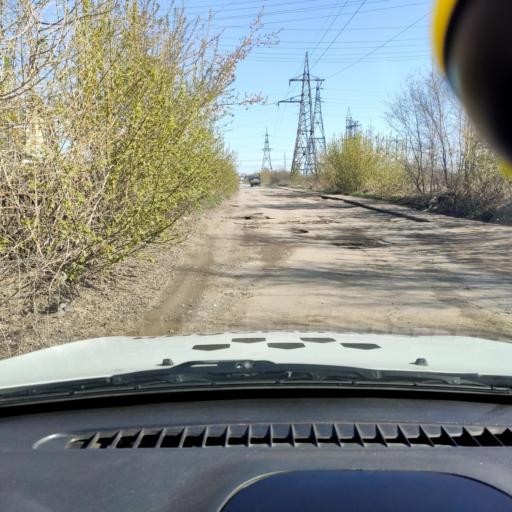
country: RU
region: Samara
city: Tol'yatti
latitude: 53.5869
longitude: 49.2952
